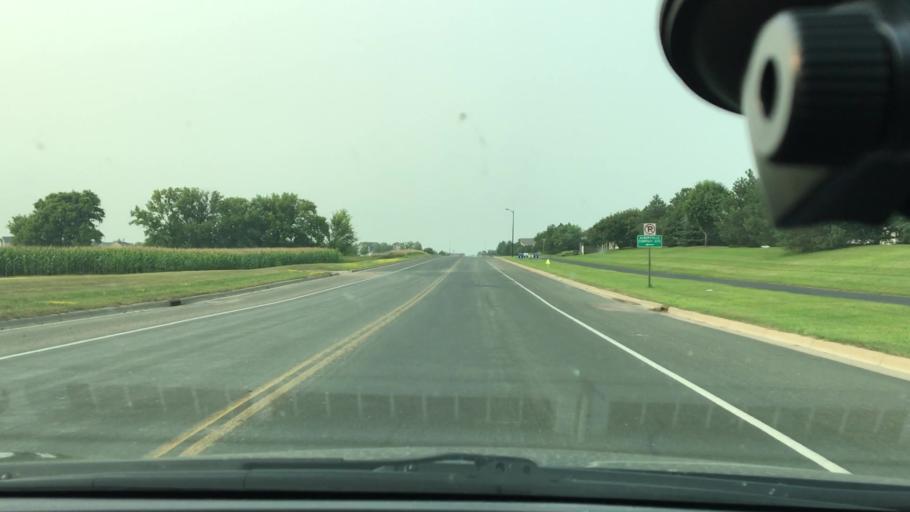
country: US
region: Minnesota
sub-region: Wright County
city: Albertville
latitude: 45.2440
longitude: -93.6428
